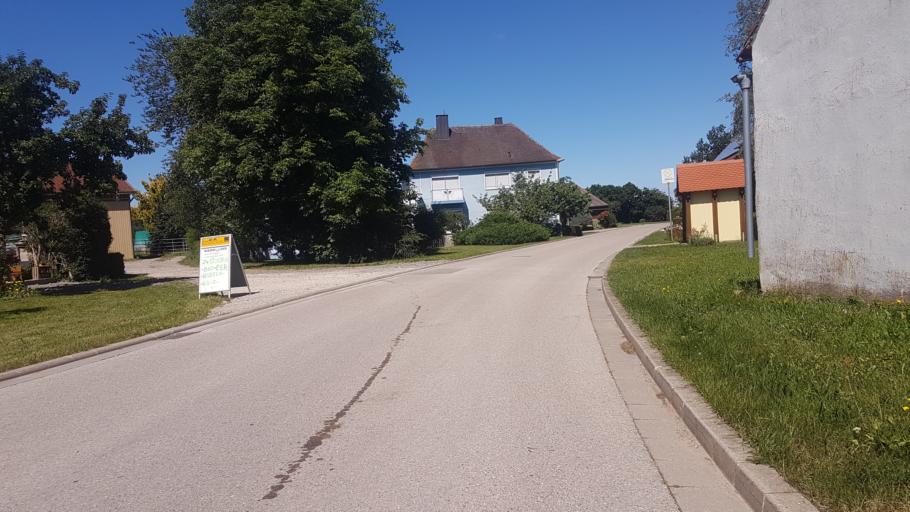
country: DE
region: Bavaria
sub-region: Regierungsbezirk Mittelfranken
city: Herrieden
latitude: 49.2201
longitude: 10.5240
